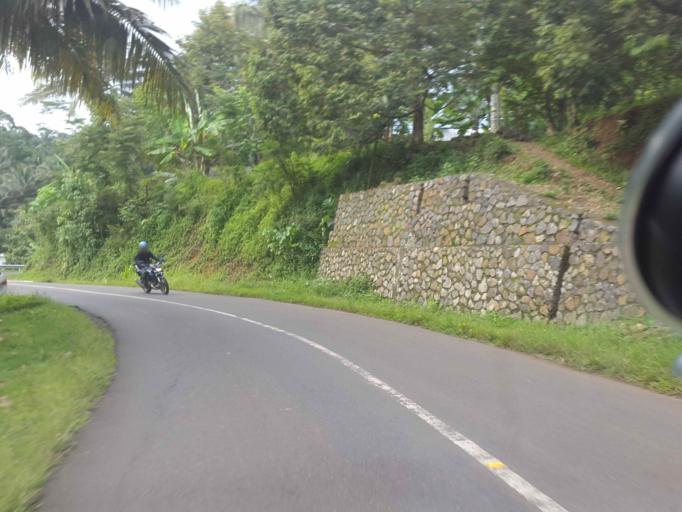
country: ID
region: Central Java
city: Banyumas
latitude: -7.5661
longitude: 109.3167
